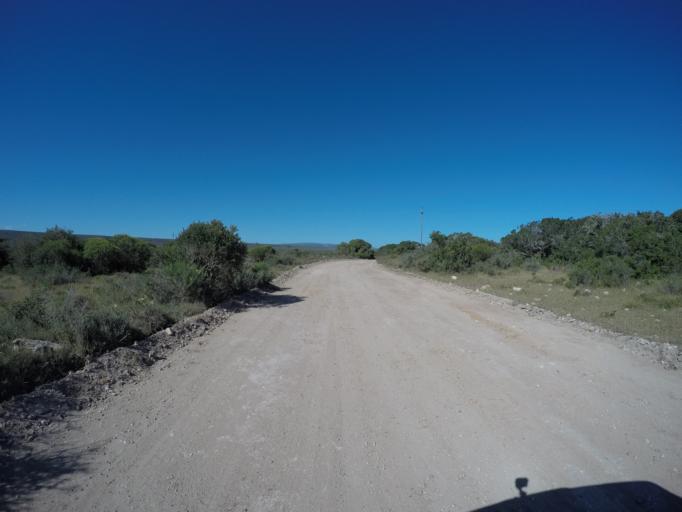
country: ZA
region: Western Cape
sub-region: Overberg District Municipality
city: Bredasdorp
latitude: -34.4524
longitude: 20.4047
